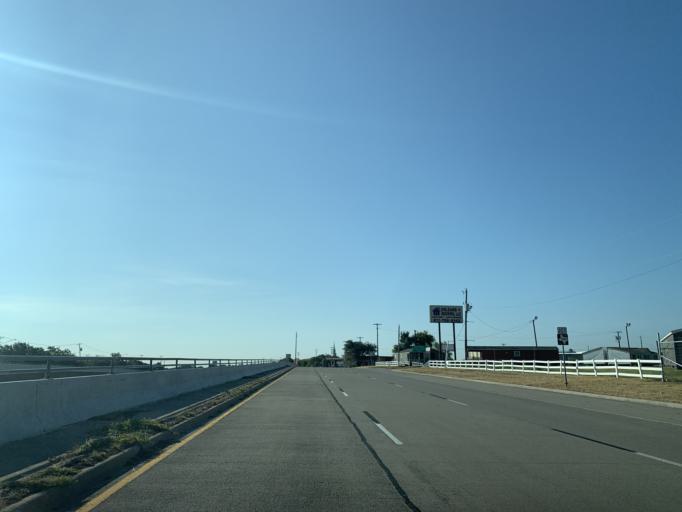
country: US
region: Texas
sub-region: Tarrant County
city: Lakeside
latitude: 32.8281
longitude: -97.4819
